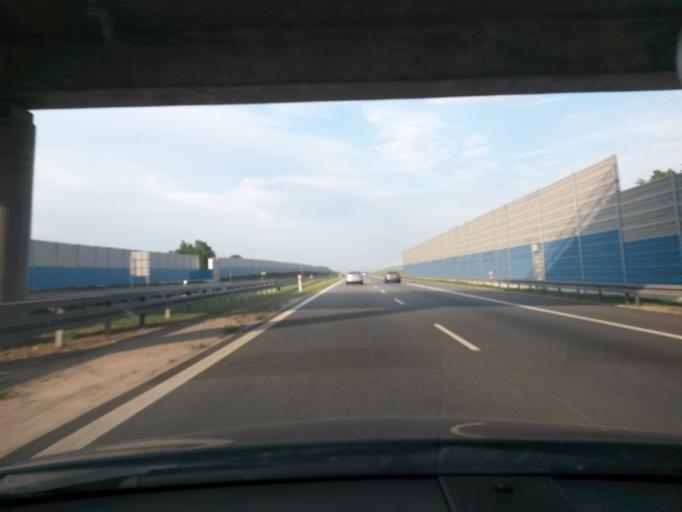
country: PL
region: Lodz Voivodeship
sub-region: Powiat brzezinski
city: Dmosin
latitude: 51.9232
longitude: 19.7753
